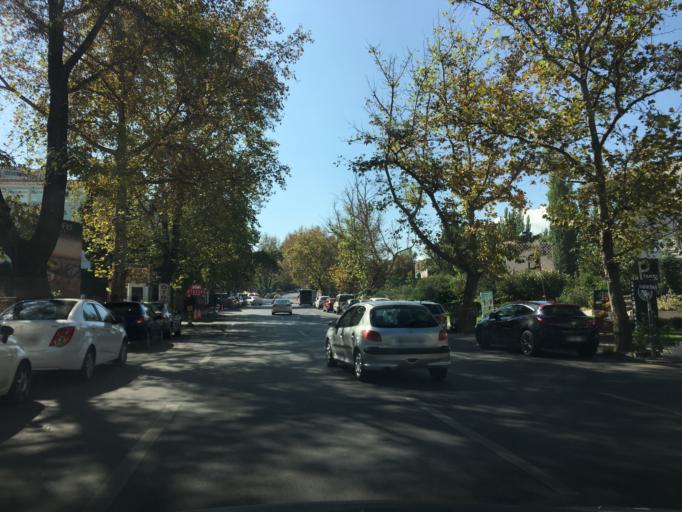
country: TR
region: Ankara
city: Cankaya
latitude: 39.8991
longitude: 32.8630
